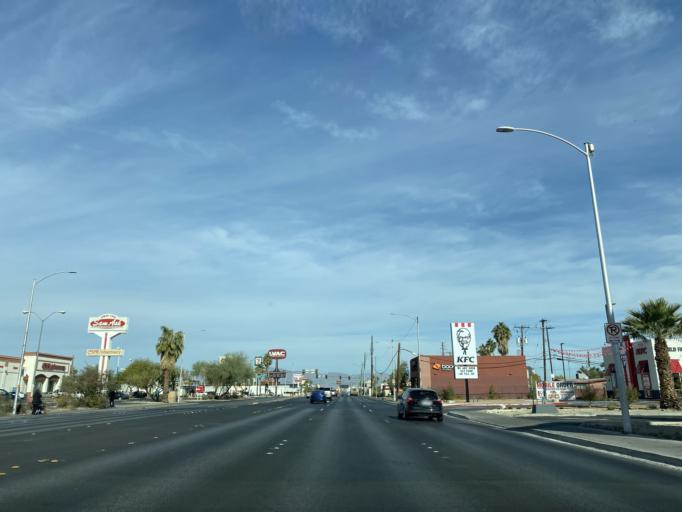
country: US
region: Nevada
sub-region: Clark County
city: Winchester
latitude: 36.1392
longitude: -115.1368
